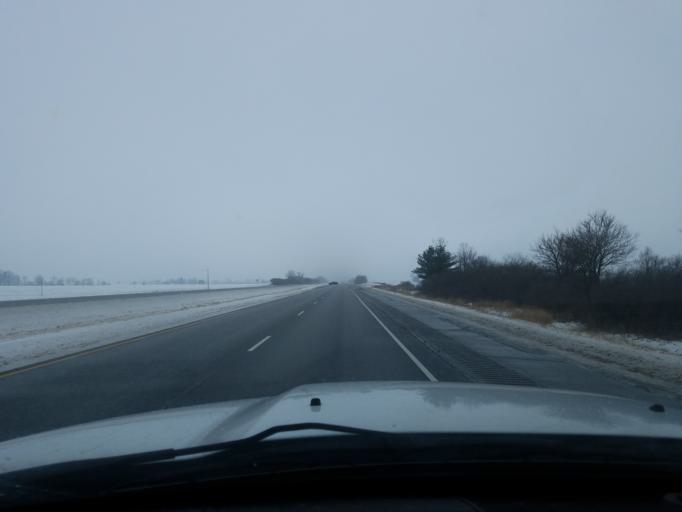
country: US
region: Indiana
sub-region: Fulton County
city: Rochester
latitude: 40.9796
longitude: -86.1679
